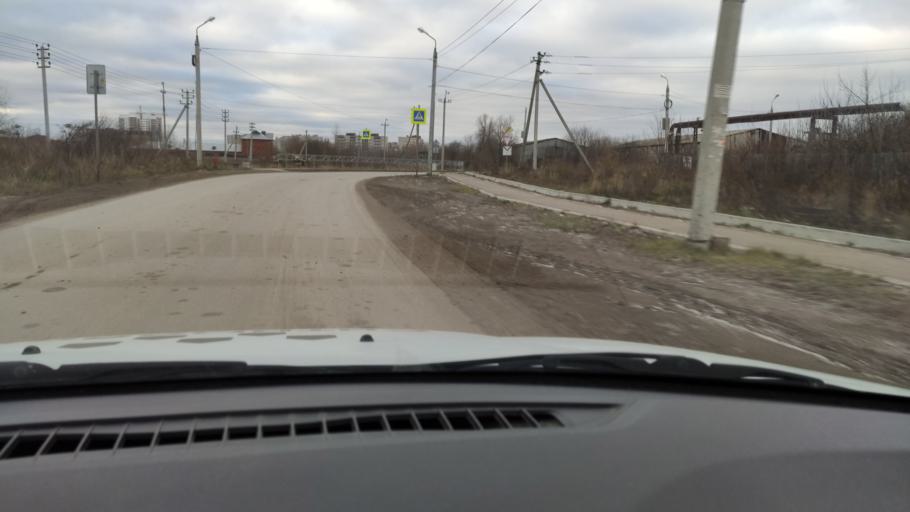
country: RU
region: Perm
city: Kondratovo
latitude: 57.9842
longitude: 56.1176
